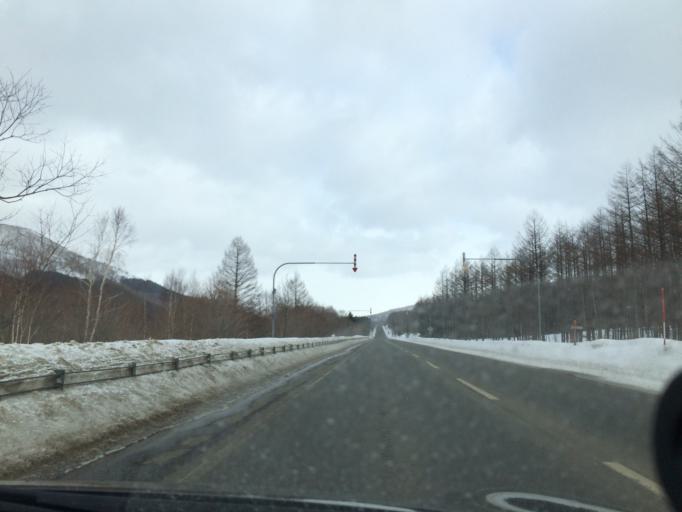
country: JP
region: Hokkaido
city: Shimo-furano
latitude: 43.1317
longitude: 142.7045
